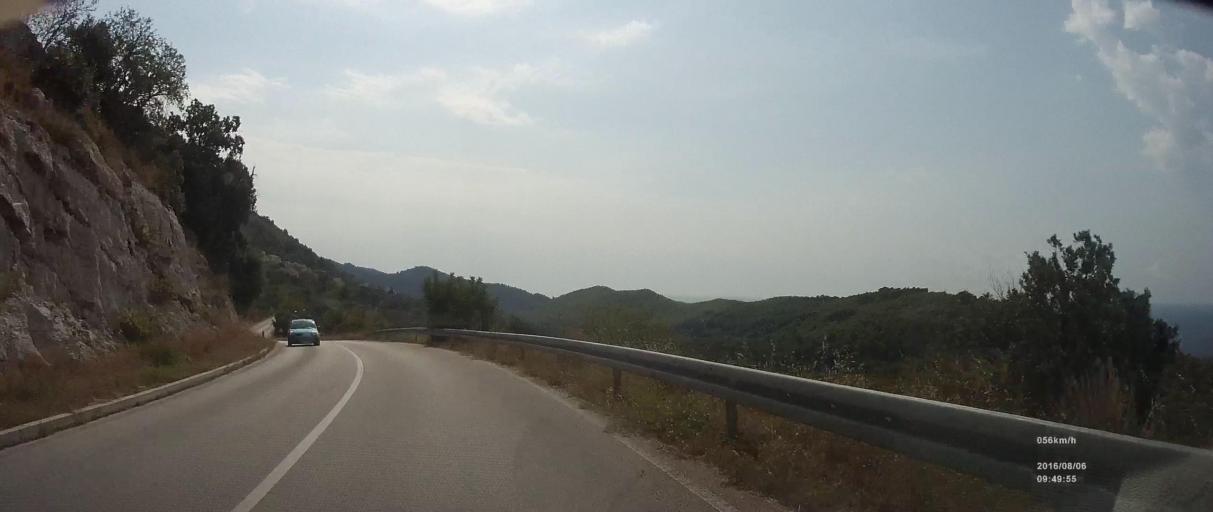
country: HR
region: Dubrovacko-Neretvanska
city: Blato
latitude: 42.7353
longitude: 17.5466
